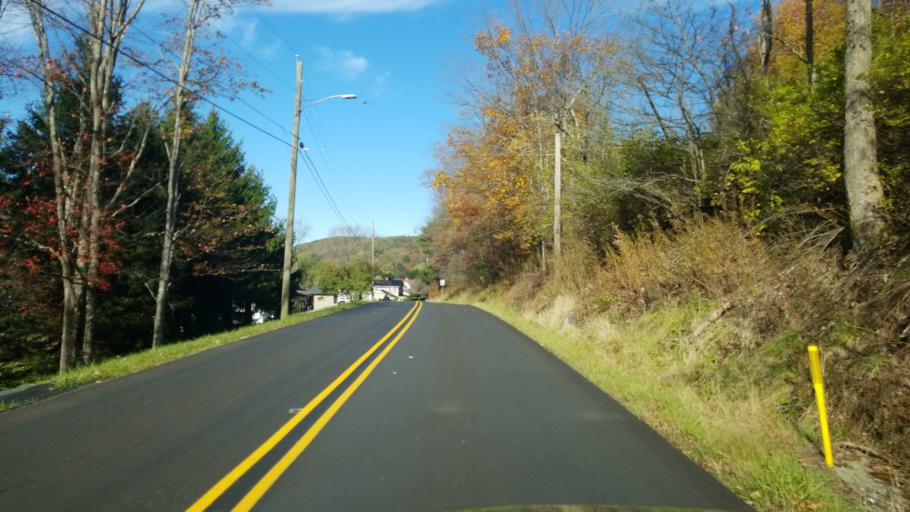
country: US
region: Pennsylvania
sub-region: Jefferson County
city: Brockway
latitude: 41.2431
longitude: -78.7963
